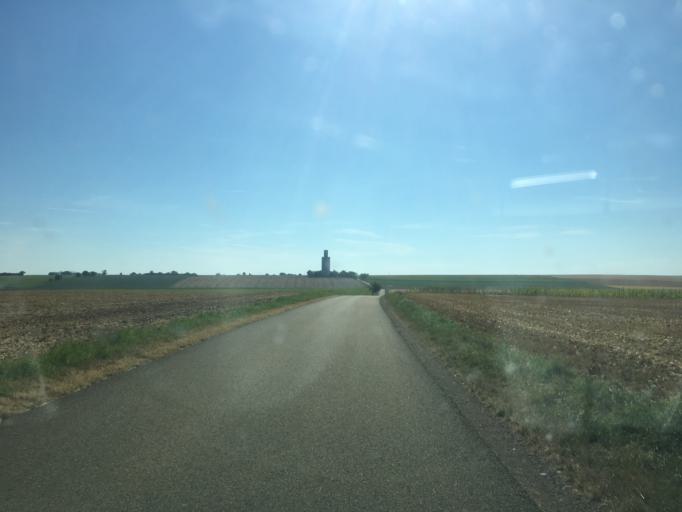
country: FR
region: Bourgogne
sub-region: Departement de l'Yonne
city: Fleury-la-Vallee
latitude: 47.9172
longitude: 3.4142
